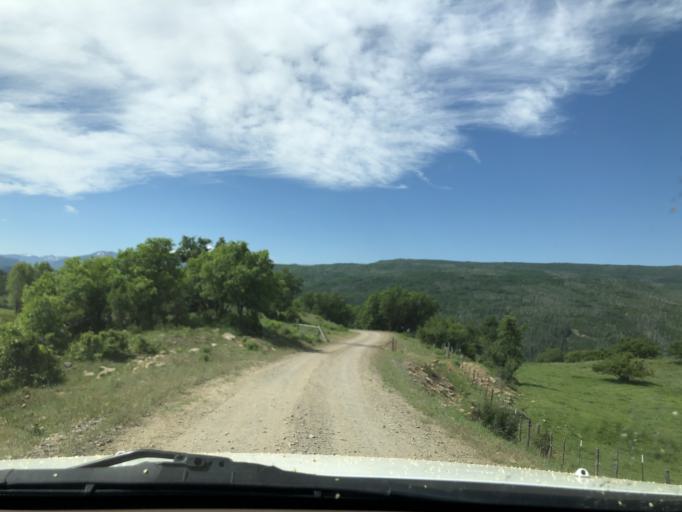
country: US
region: Colorado
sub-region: Delta County
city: Paonia
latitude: 39.0021
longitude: -107.3458
